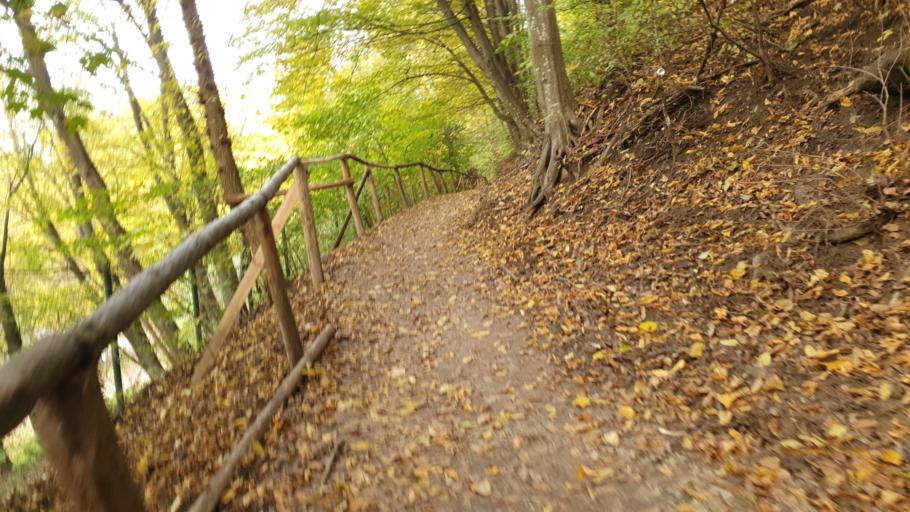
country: PL
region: Lublin Voivodeship
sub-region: Powiat pulawski
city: Kazimierz Dolny
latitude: 51.3226
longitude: 21.9509
